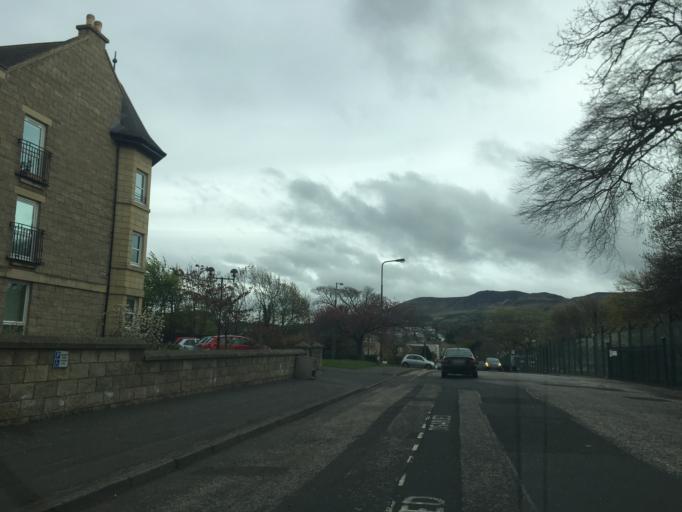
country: GB
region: Scotland
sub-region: Edinburgh
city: Colinton
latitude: 55.9143
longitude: -3.2397
